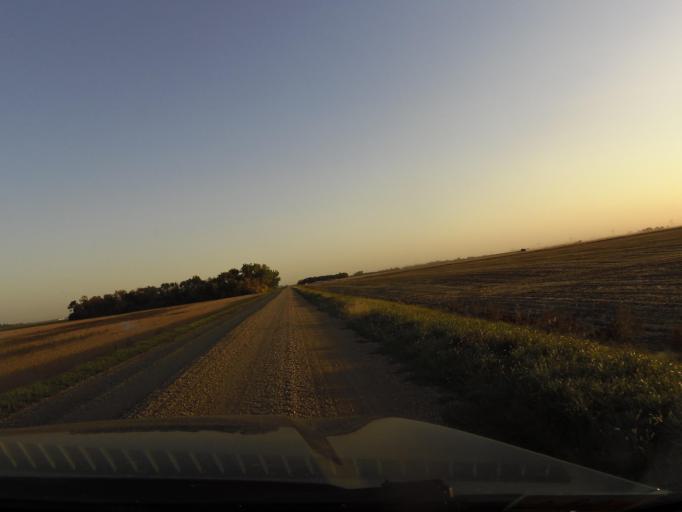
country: US
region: North Dakota
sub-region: Walsh County
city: Grafton
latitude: 48.3932
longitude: -97.2556
